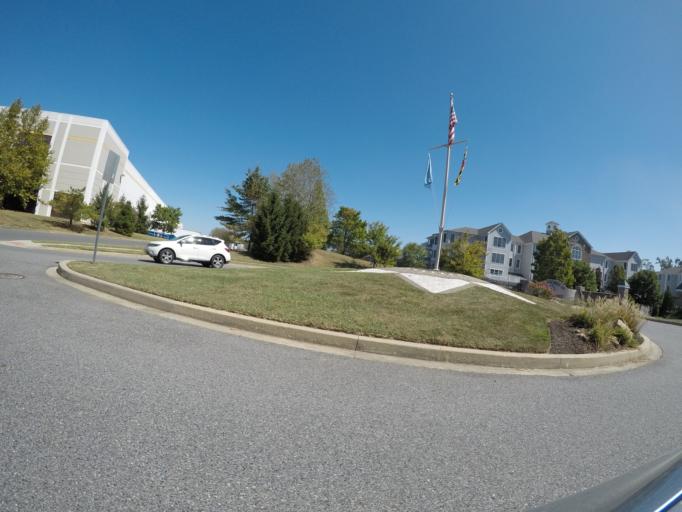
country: US
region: Maryland
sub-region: Harford County
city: Riverside
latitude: 39.4669
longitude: -76.2340
